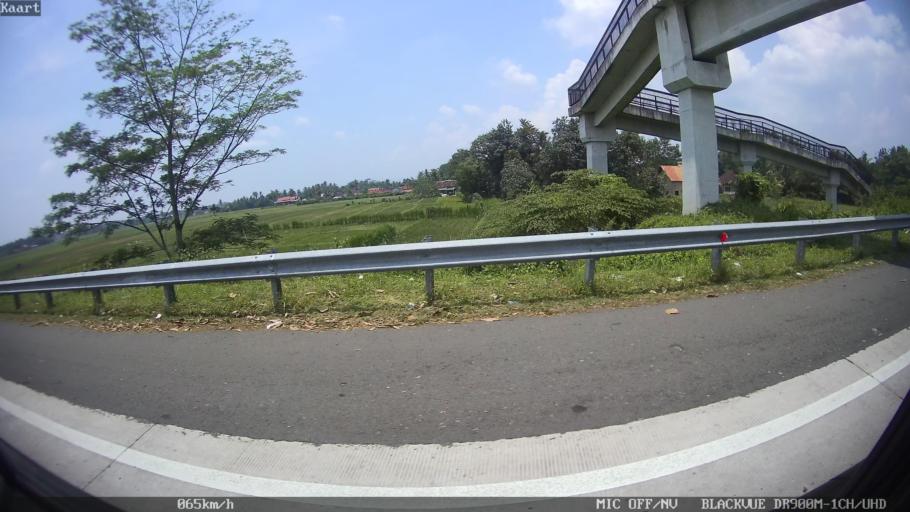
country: ID
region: Lampung
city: Natar
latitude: -5.2920
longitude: 105.2306
